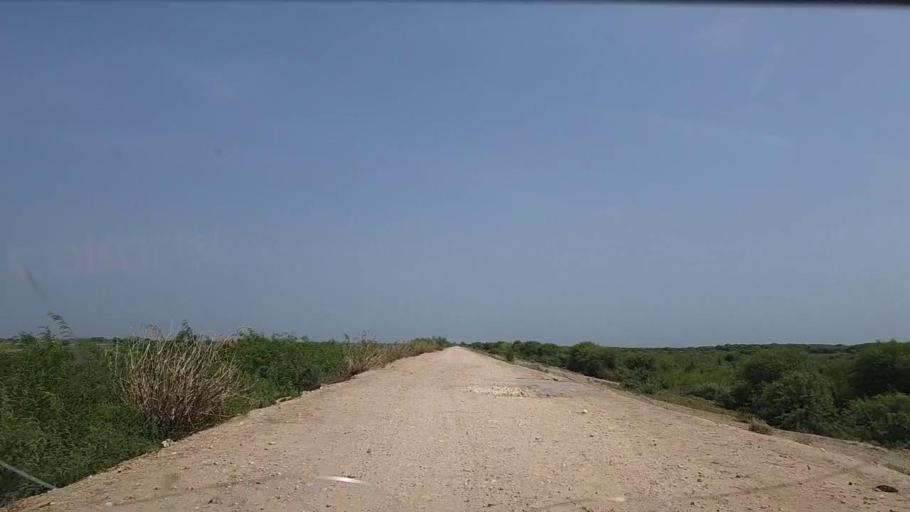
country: PK
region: Sindh
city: Ghotki
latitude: 28.1114
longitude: 69.3921
